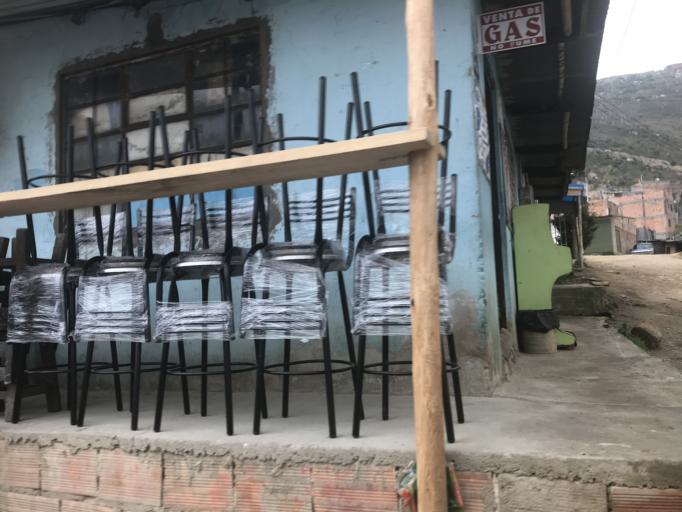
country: CO
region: Cundinamarca
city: Soacha
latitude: 4.5554
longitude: -74.2119
